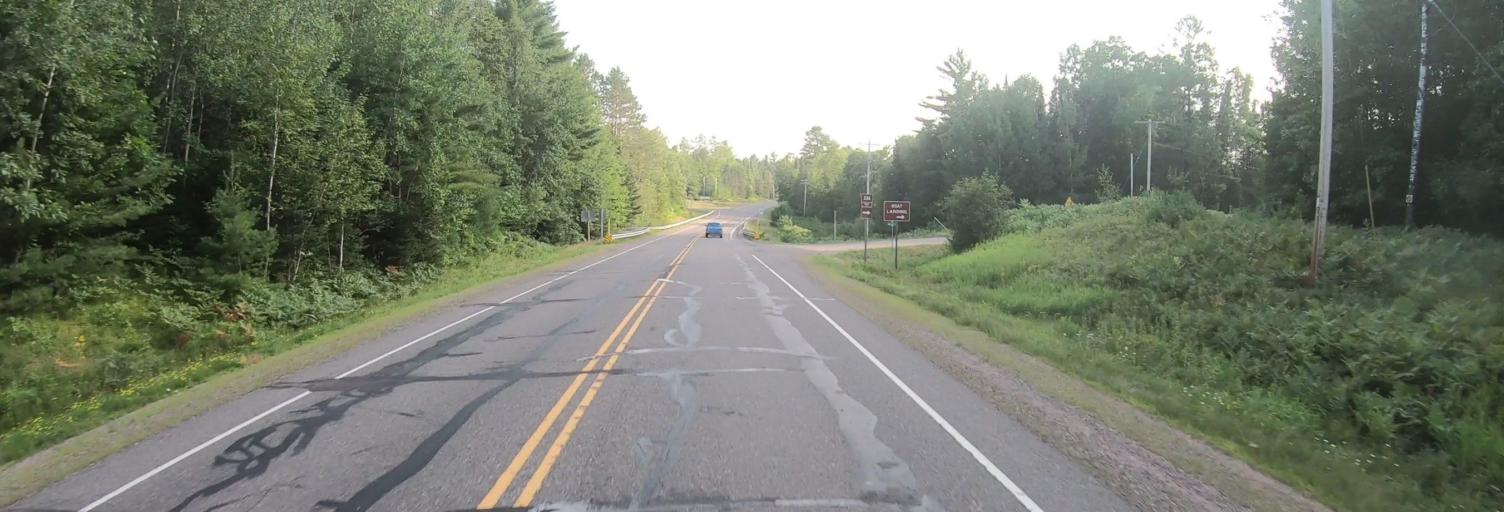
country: US
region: Wisconsin
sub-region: Ashland County
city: Ashland
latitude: 46.1552
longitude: -90.9150
